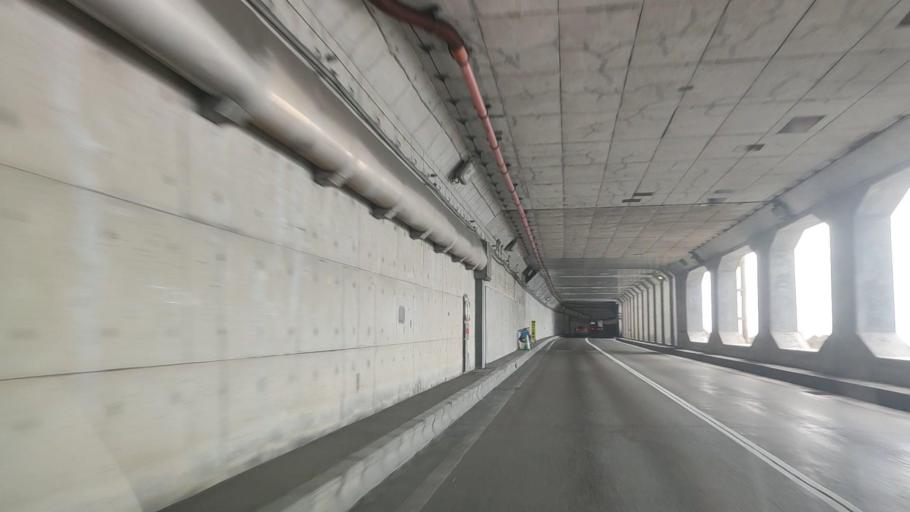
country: JP
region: Hokkaido
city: Rumoi
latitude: 43.8009
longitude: 141.3813
